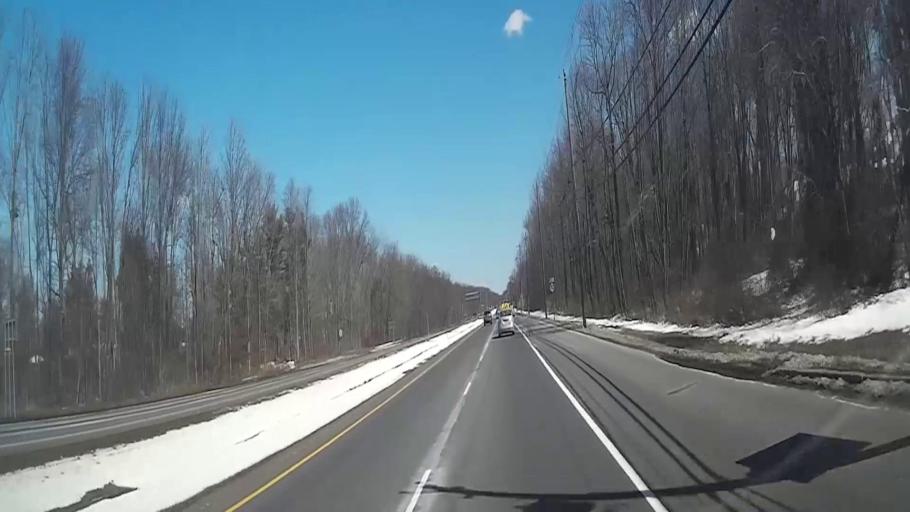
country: US
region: New Jersey
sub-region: Burlington County
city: Marlton
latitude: 39.8939
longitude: -74.9102
